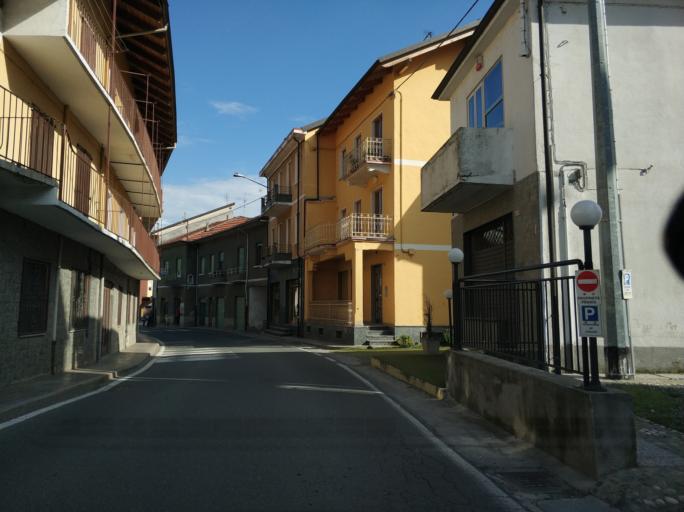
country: IT
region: Piedmont
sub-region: Provincia di Torino
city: Cafasse
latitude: 45.2485
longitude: 7.5154
